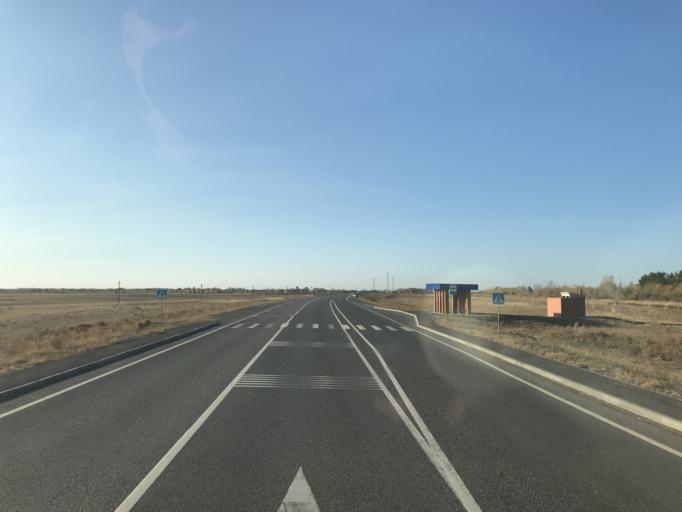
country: KZ
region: Pavlodar
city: Koktobe
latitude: 51.9102
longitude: 77.3562
